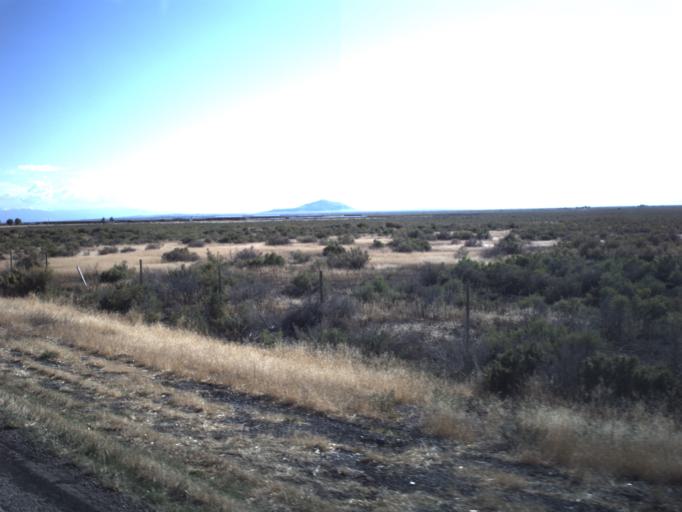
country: US
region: Utah
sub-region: Millard County
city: Delta
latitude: 39.3281
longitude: -112.4858
